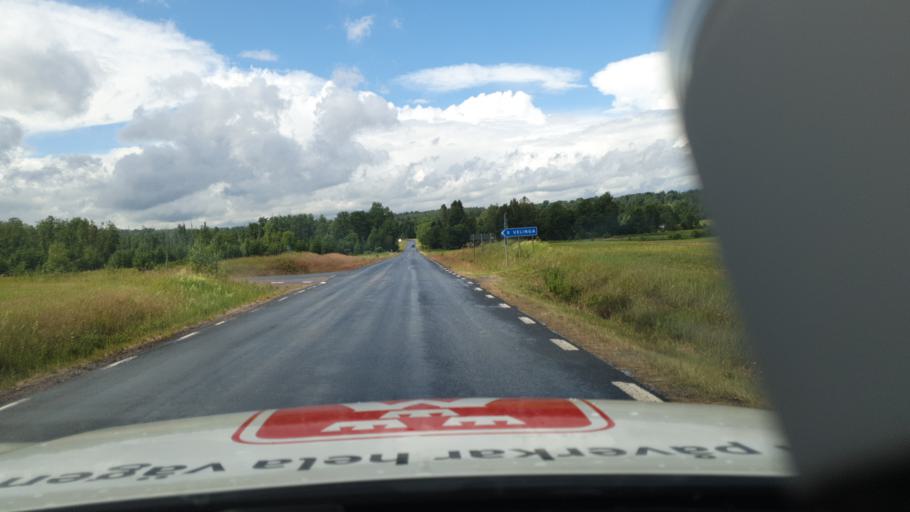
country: SE
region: Vaestra Goetaland
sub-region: Tidaholms Kommun
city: Tidaholm
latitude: 58.1391
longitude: 14.0138
